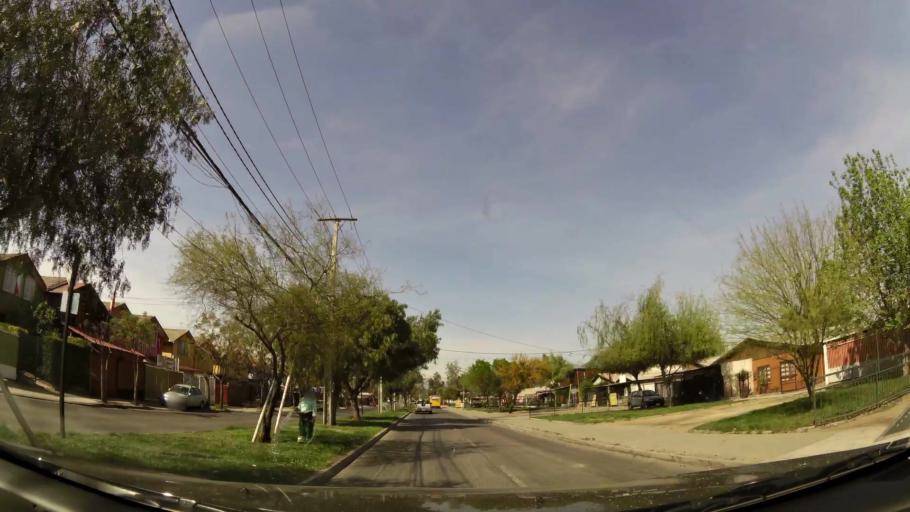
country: CL
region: Santiago Metropolitan
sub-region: Provincia de Cordillera
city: Puente Alto
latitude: -33.6118
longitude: -70.5875
